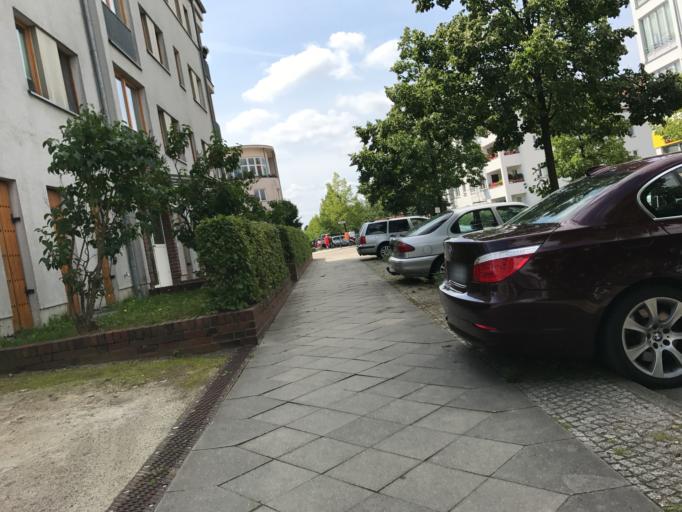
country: DE
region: Berlin
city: Karow
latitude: 52.6218
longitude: 13.4858
